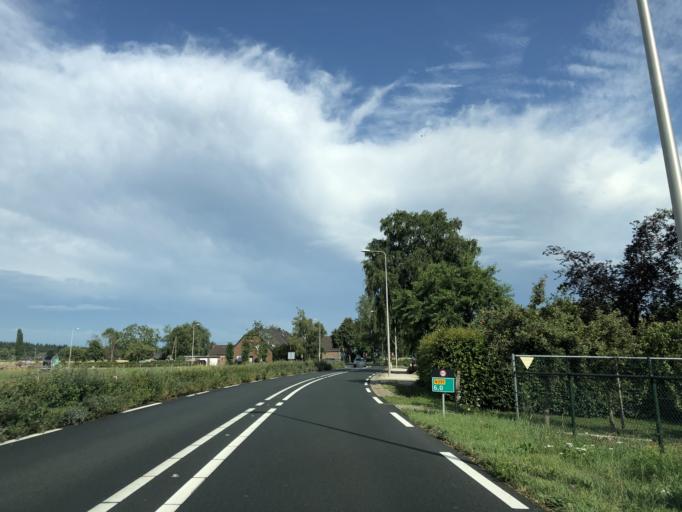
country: NL
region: Limburg
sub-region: Gemeente Gennep
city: Gennep
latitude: 51.7146
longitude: 6.0411
